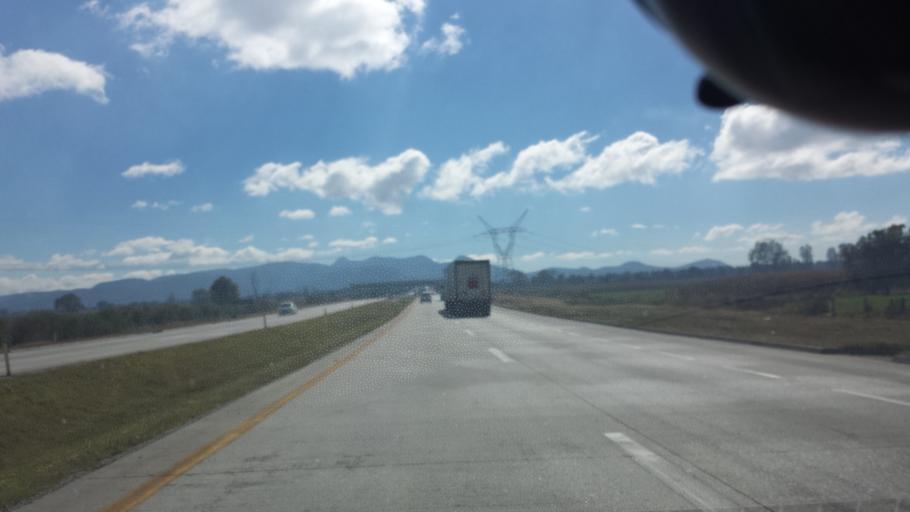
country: MX
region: Hidalgo
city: Doxey
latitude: 20.0951
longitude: -99.2729
